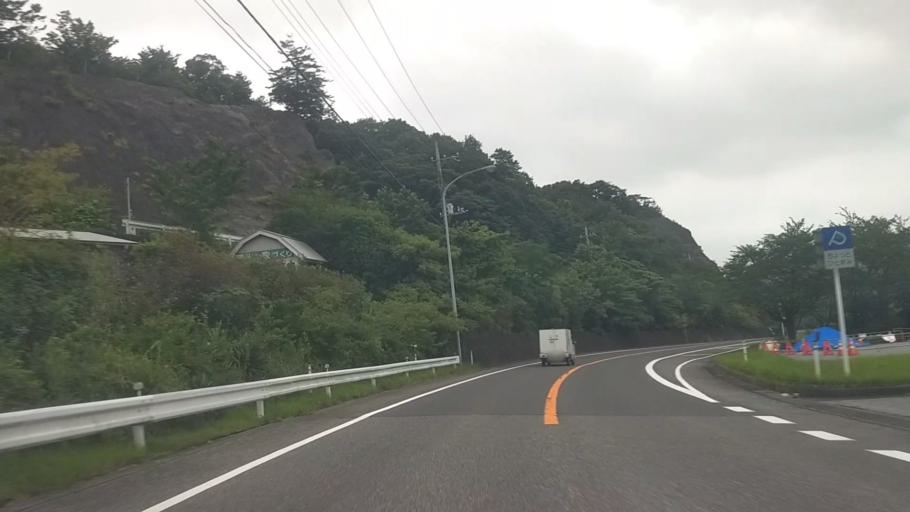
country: JP
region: Chiba
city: Kawaguchi
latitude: 35.1647
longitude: 140.0623
